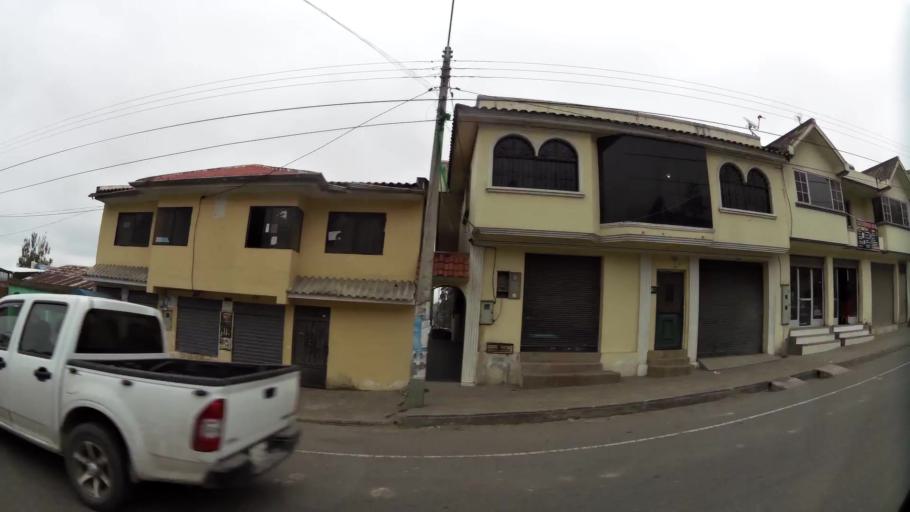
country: EC
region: Canar
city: Canar
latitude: -2.5057
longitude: -78.9251
